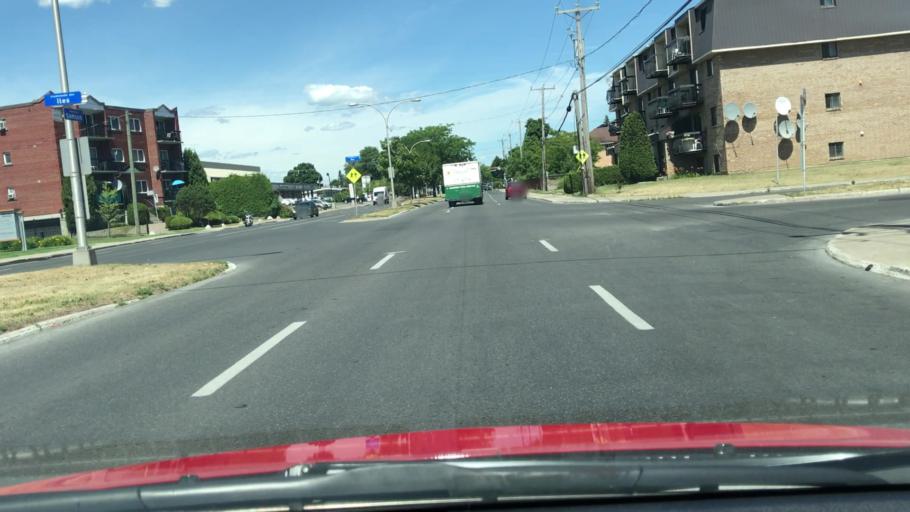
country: CA
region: Quebec
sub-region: Laval
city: Laval
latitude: 45.5314
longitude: -73.7531
